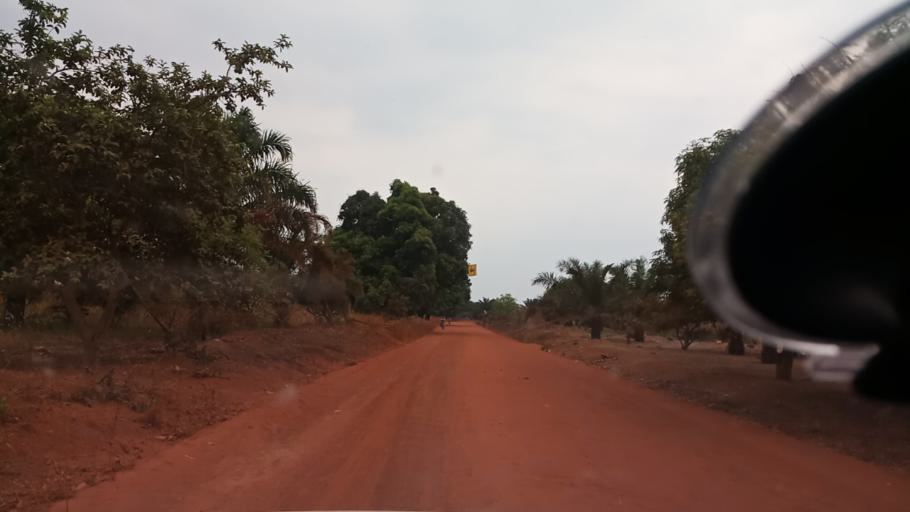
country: ZM
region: Luapula
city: Nchelenge
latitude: -9.1608
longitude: 28.2826
